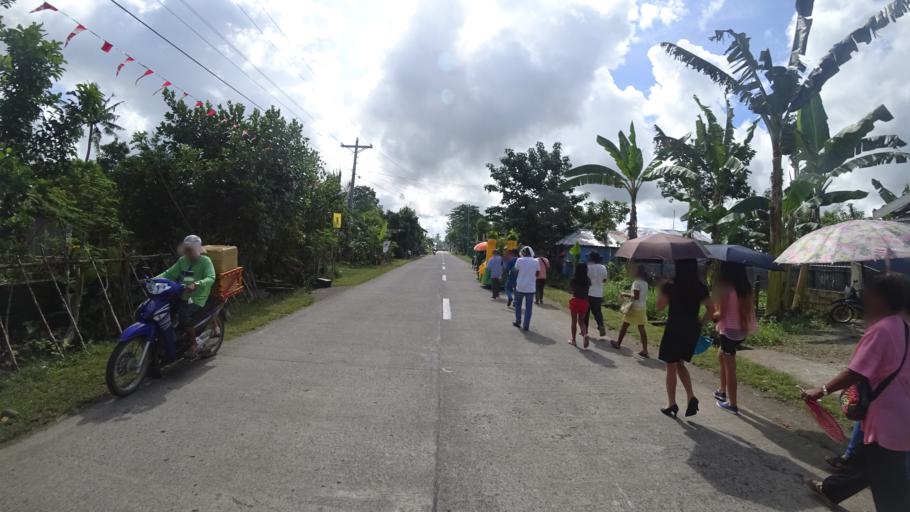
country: PH
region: Eastern Visayas
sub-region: Province of Leyte
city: Burauen
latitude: 10.9804
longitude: 124.9195
